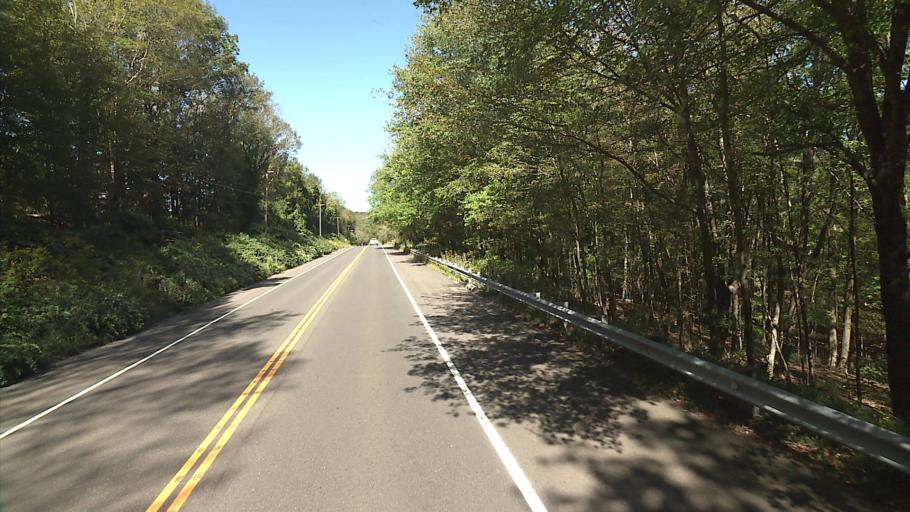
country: US
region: Connecticut
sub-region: New Haven County
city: Prospect
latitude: 41.4242
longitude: -72.9734
